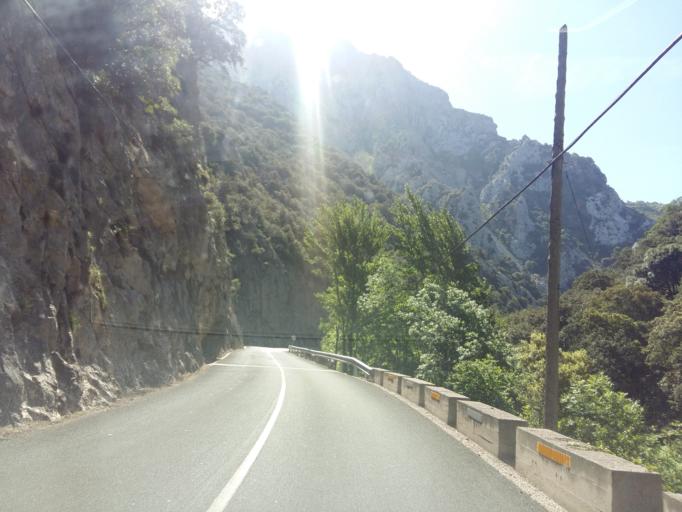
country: ES
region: Cantabria
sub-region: Provincia de Cantabria
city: Potes
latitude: 43.2035
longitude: -4.5931
